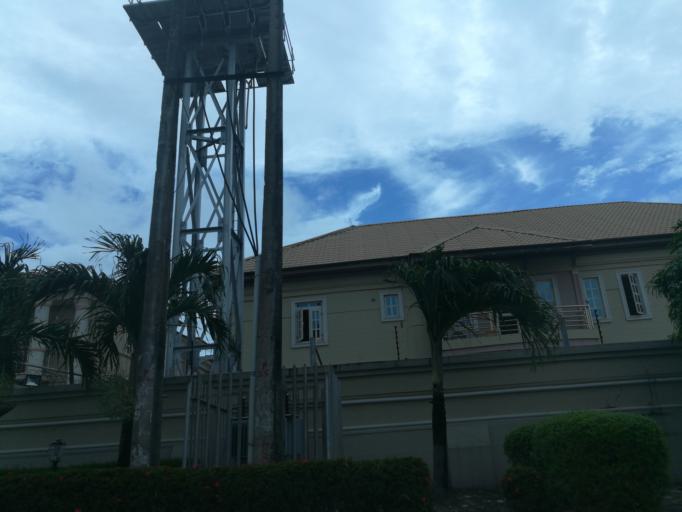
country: NG
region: Lagos
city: Ikoyi
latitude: 6.4435
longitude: 3.4735
